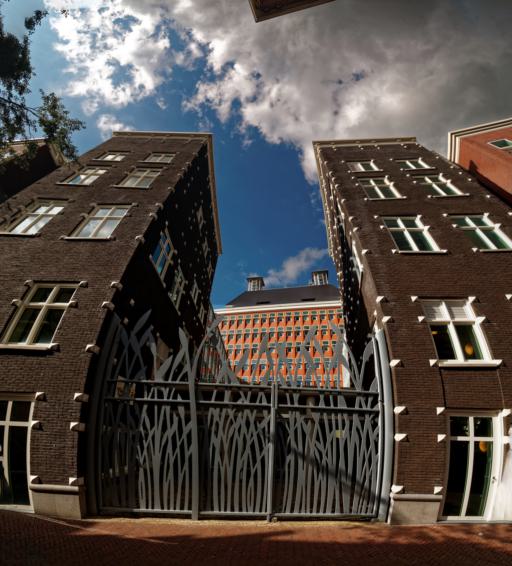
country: NL
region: Friesland
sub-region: Gemeente Leeuwarden
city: Leeuwarden
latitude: 53.2008
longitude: 5.7995
